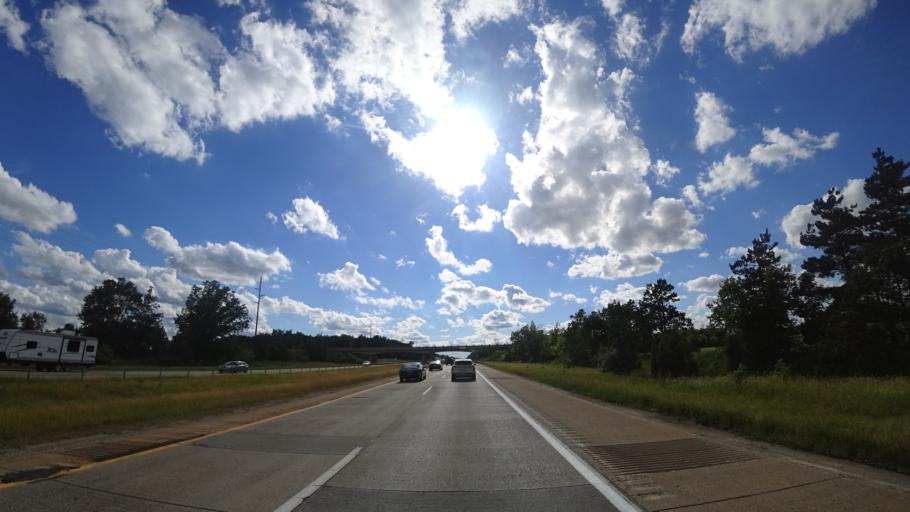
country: US
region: Michigan
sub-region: Ionia County
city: Portland
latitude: 42.8792
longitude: -84.9930
